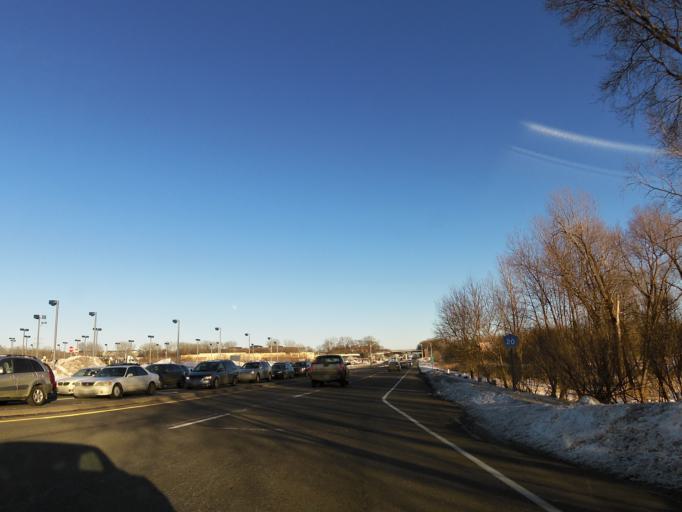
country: US
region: Minnesota
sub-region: Ramsey County
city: Vadnais Heights
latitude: 45.0280
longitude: -93.0462
